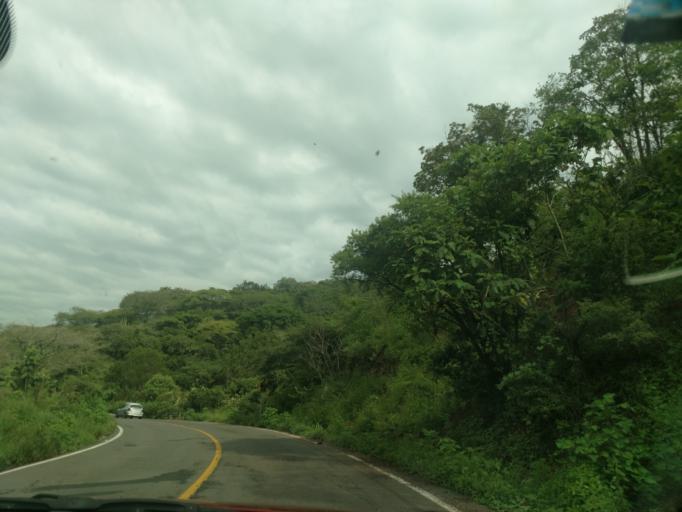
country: MX
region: Jalisco
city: Ameca
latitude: 20.5411
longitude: -104.2741
